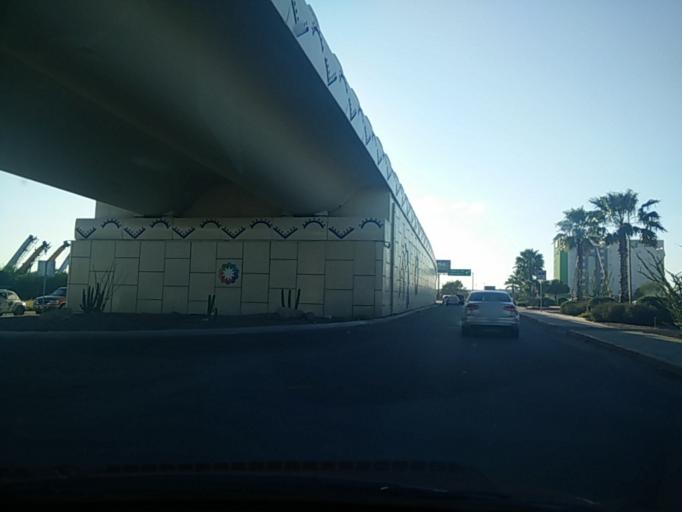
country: MX
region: Sonora
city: Hermosillo
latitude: 29.0956
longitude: -111.0229
